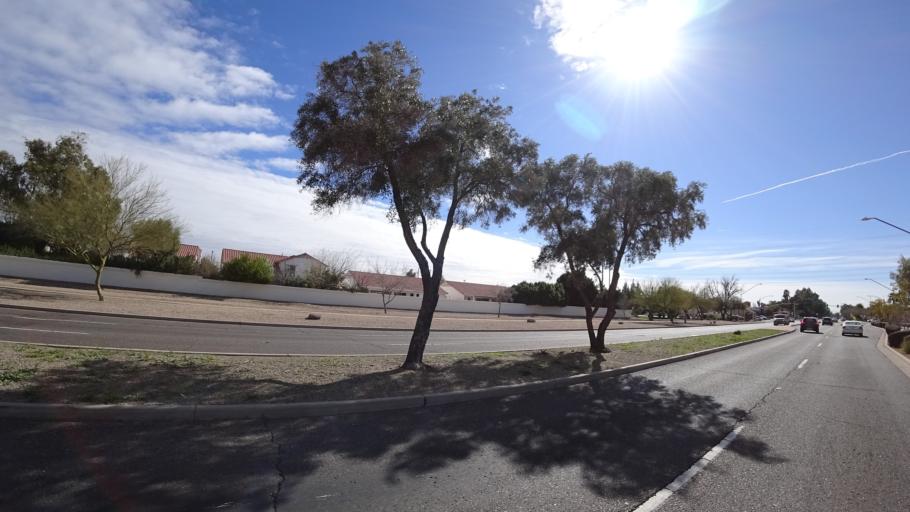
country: US
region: Arizona
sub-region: Maricopa County
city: Peoria
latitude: 33.5980
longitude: -112.1861
